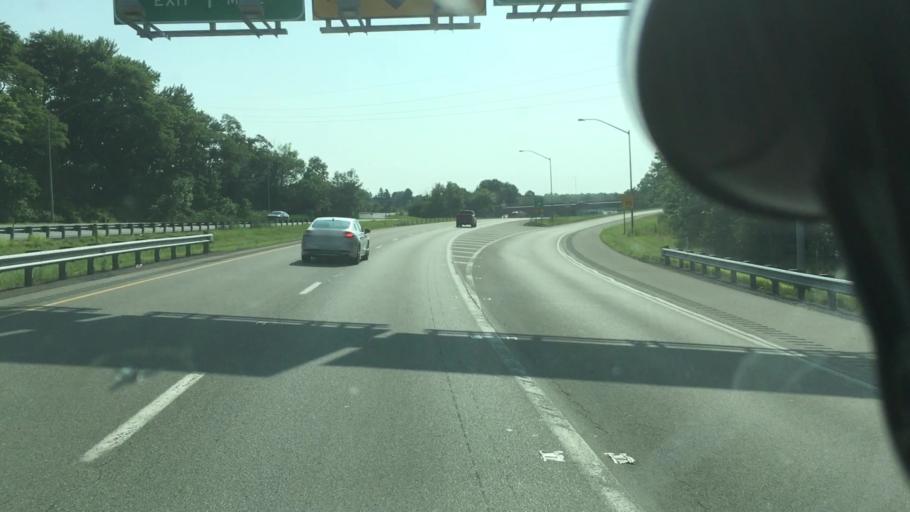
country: US
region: Pennsylvania
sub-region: Lawrence County
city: New Castle
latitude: 40.9721
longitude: -80.3189
